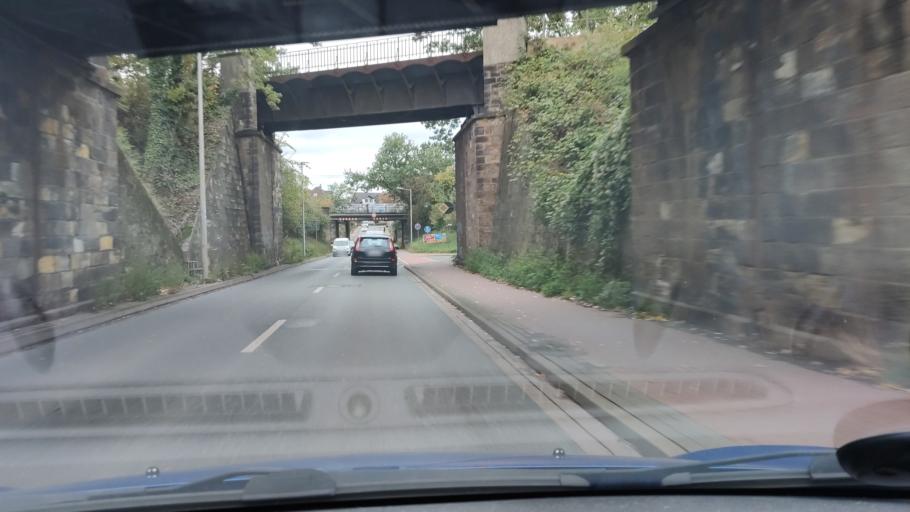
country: DE
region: Lower Saxony
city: Seelze
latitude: 52.3937
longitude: 9.6501
